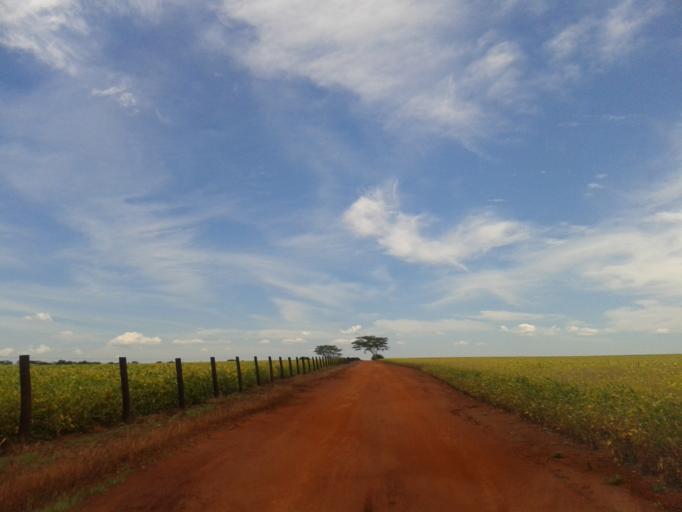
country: BR
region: Minas Gerais
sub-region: Capinopolis
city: Capinopolis
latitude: -18.6698
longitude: -49.7255
